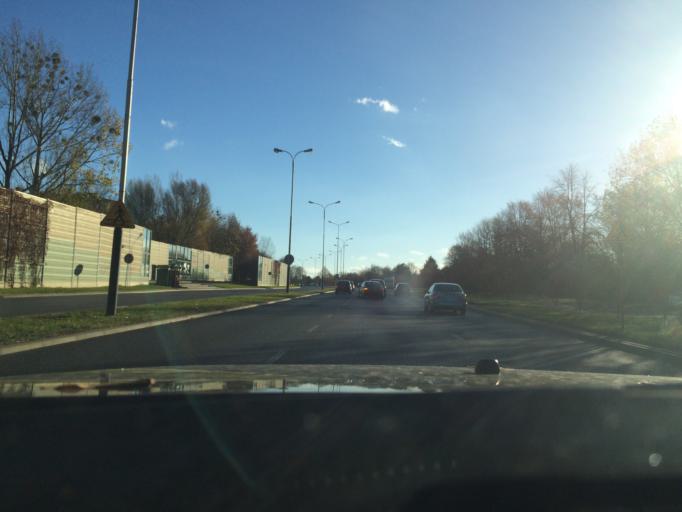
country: PL
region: Lodz Voivodeship
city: Lodz
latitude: 51.7336
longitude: 19.4419
